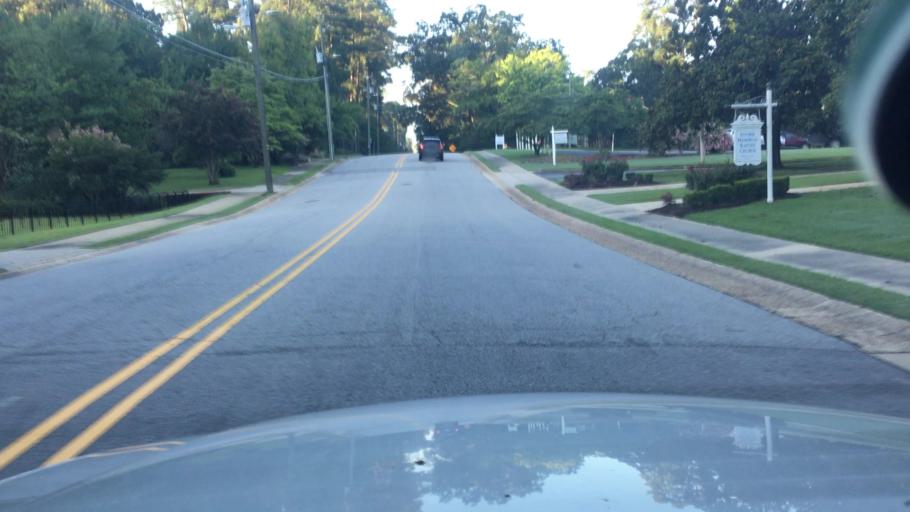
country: US
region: North Carolina
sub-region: Cumberland County
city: Fayetteville
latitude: 35.0663
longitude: -78.9049
